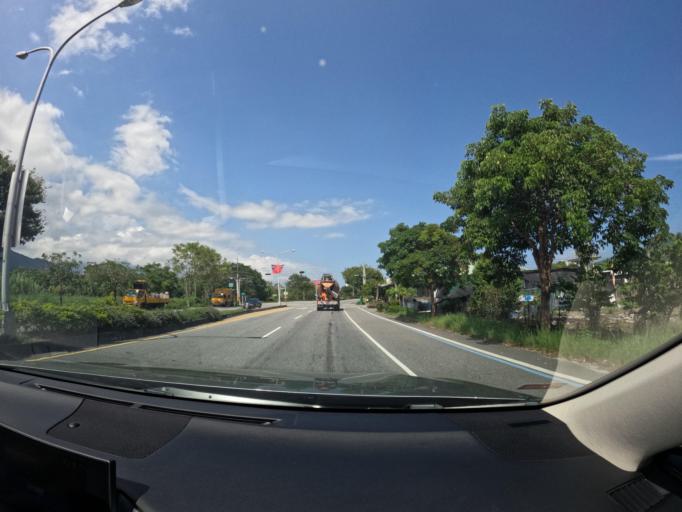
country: TW
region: Taiwan
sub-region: Hualien
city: Hualian
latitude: 23.8872
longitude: 121.5459
